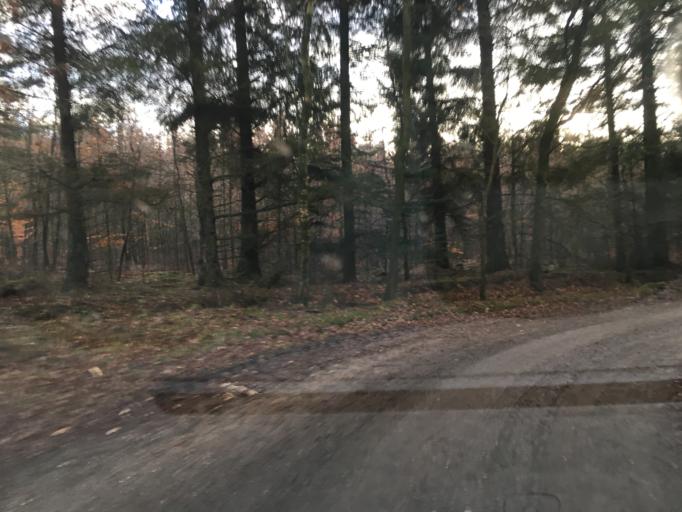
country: DK
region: South Denmark
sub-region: Tonder Kommune
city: Logumkloster
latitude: 55.1271
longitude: 8.8817
